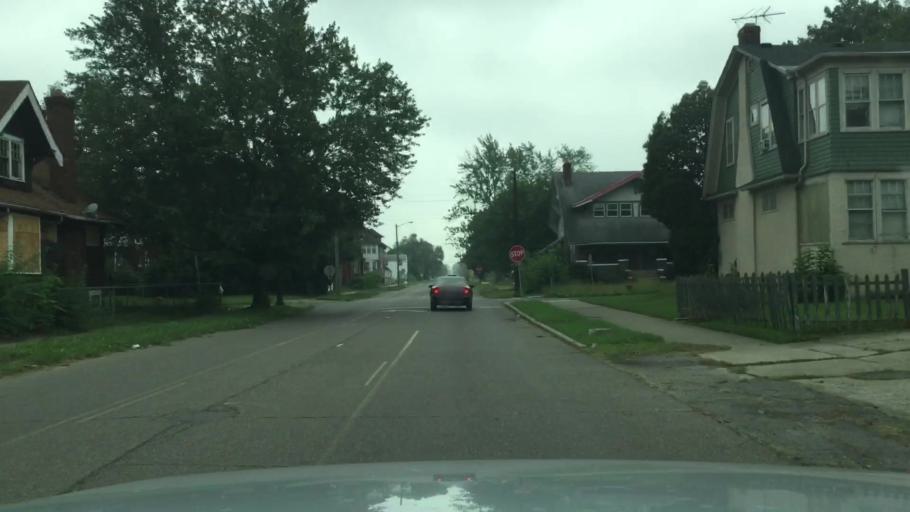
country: US
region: Michigan
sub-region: Wayne County
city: Highland Park
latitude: 42.4118
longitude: -83.1088
